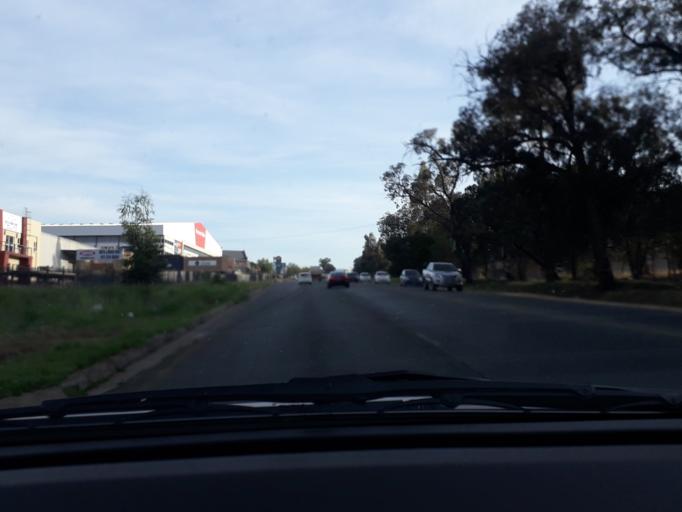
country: ZA
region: Gauteng
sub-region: City of Johannesburg Metropolitan Municipality
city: Midrand
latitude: -25.9522
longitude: 28.1413
